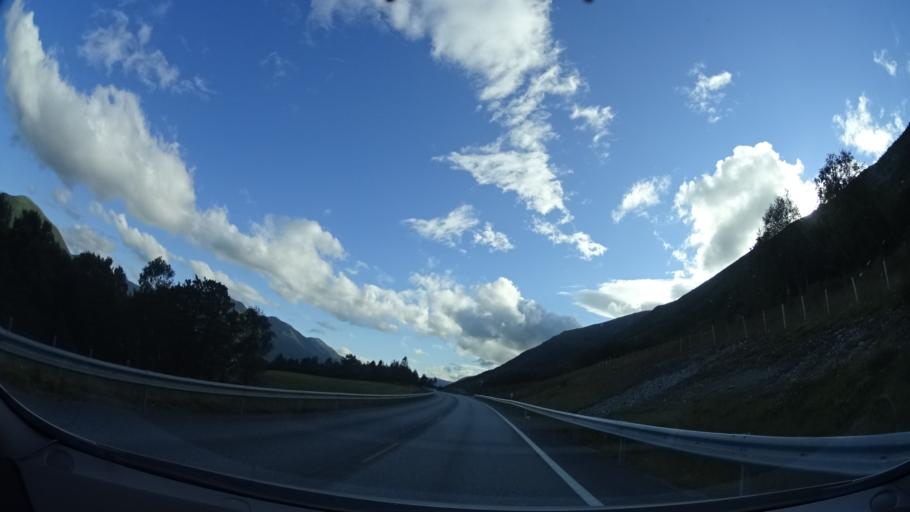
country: NO
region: More og Romsdal
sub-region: Gjemnes
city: Batnfjordsora
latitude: 62.9500
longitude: 7.7566
